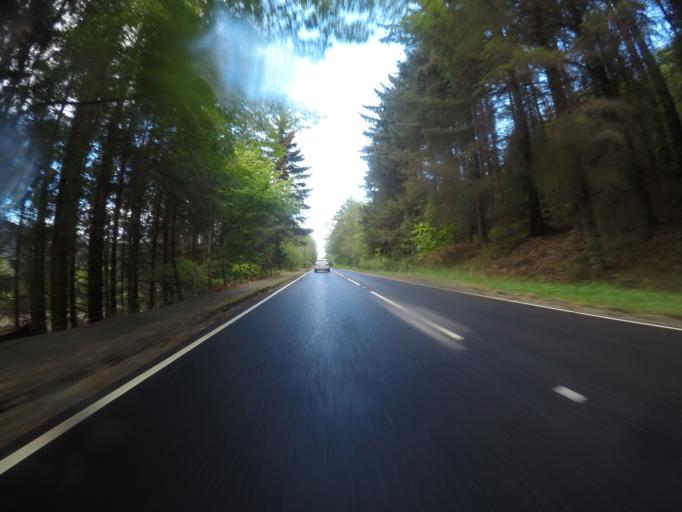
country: GB
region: Scotland
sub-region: Highland
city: Fort William
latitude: 57.2382
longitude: -5.4405
